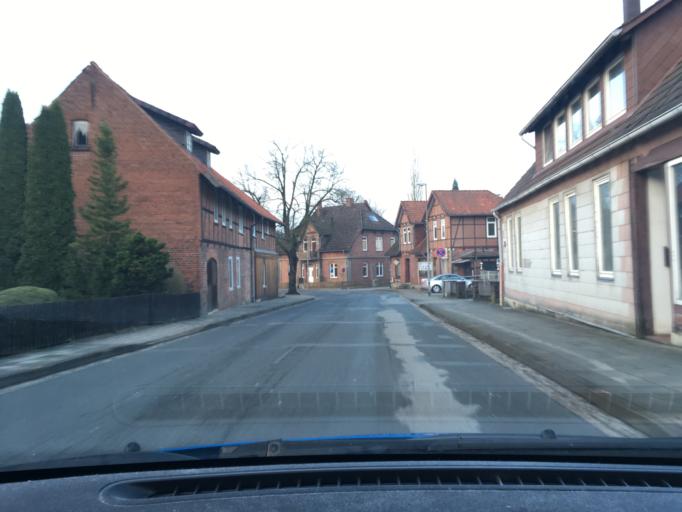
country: DE
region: Lower Saxony
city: Bad Fallingbostel
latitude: 52.9011
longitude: 9.7696
